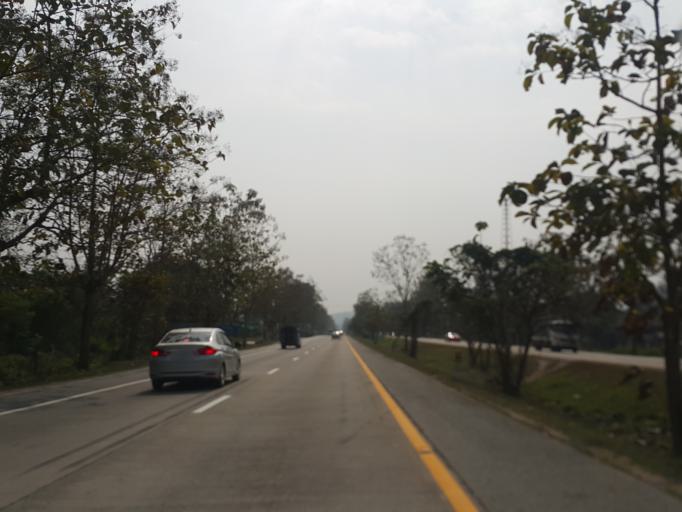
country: TH
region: Lamphun
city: Mae Tha
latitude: 18.5257
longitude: 99.0835
